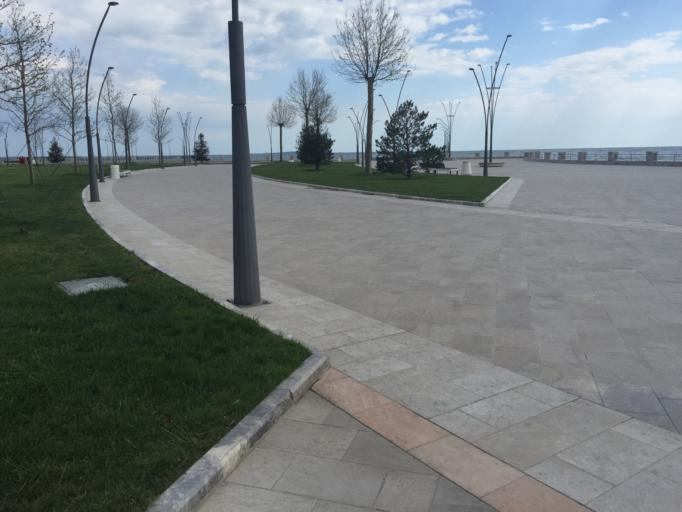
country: AZ
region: Baki
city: Baku
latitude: 40.3751
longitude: 49.8795
